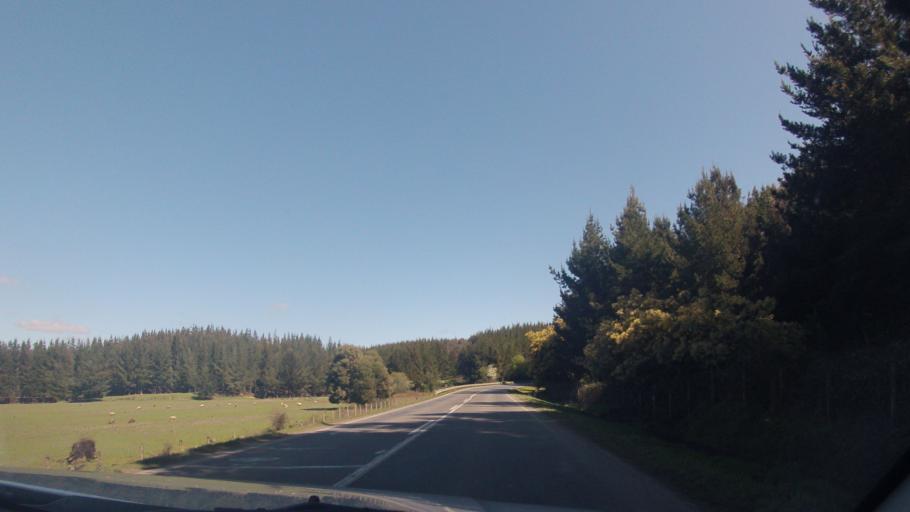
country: CL
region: Araucania
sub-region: Provincia de Malleco
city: Traiguen
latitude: -38.1681
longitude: -72.9176
